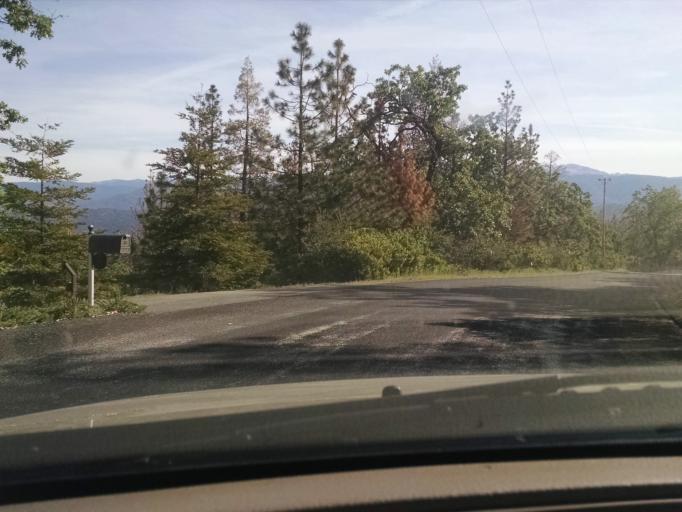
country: US
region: California
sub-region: Madera County
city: Oakhurst
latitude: 37.2858
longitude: -119.6259
